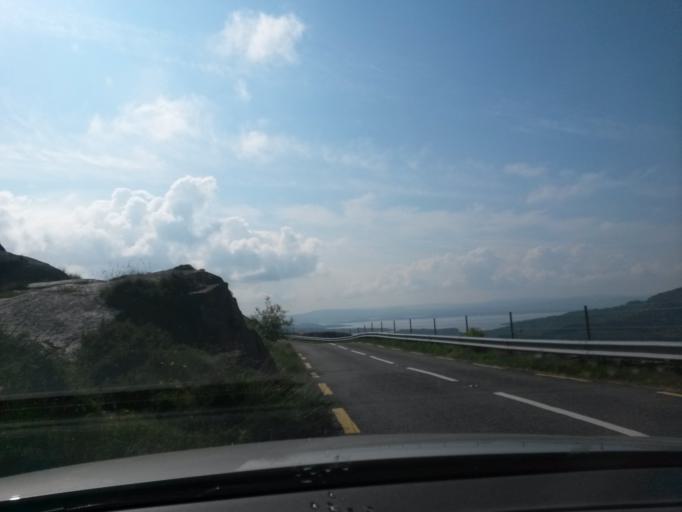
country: IE
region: Munster
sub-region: Ciarrai
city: Kenmare
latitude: 51.7706
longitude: -9.5828
